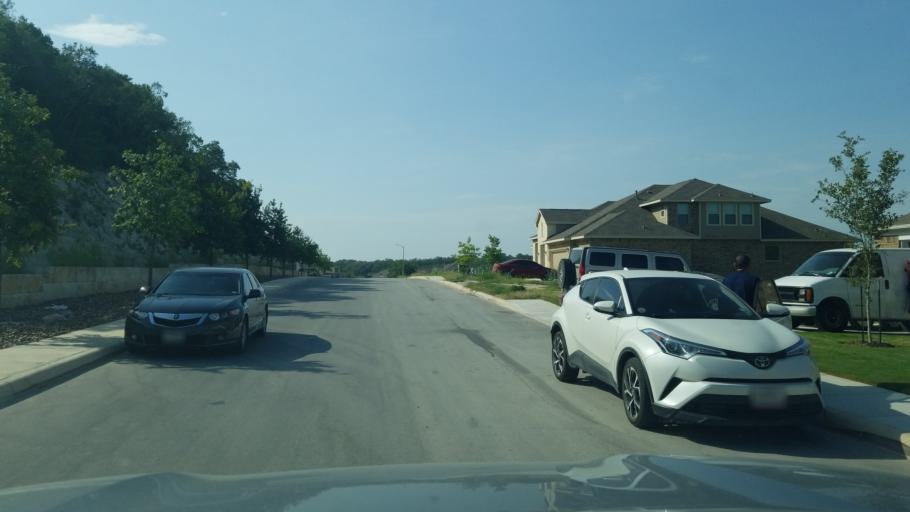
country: US
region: Texas
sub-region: Medina County
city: La Coste
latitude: 29.4041
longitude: -98.7866
